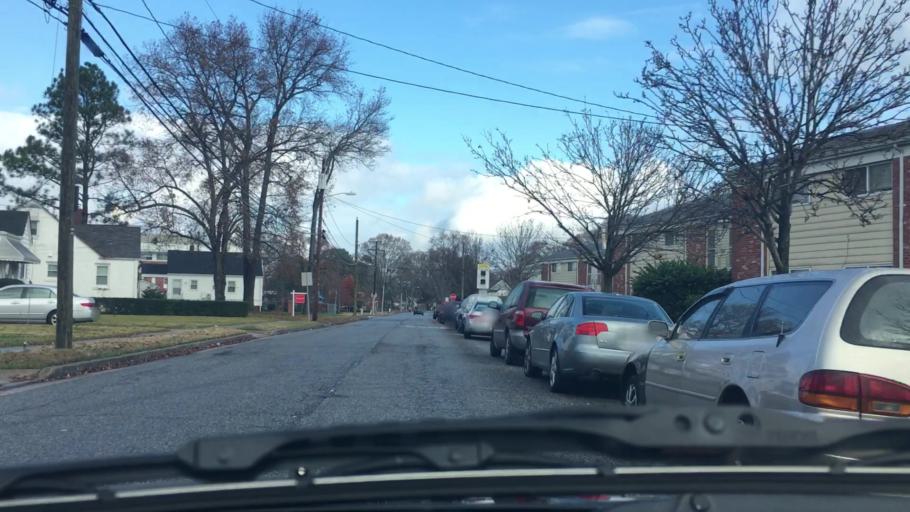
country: US
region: Virginia
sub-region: City of Norfolk
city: Norfolk
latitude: 36.9165
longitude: -76.2514
